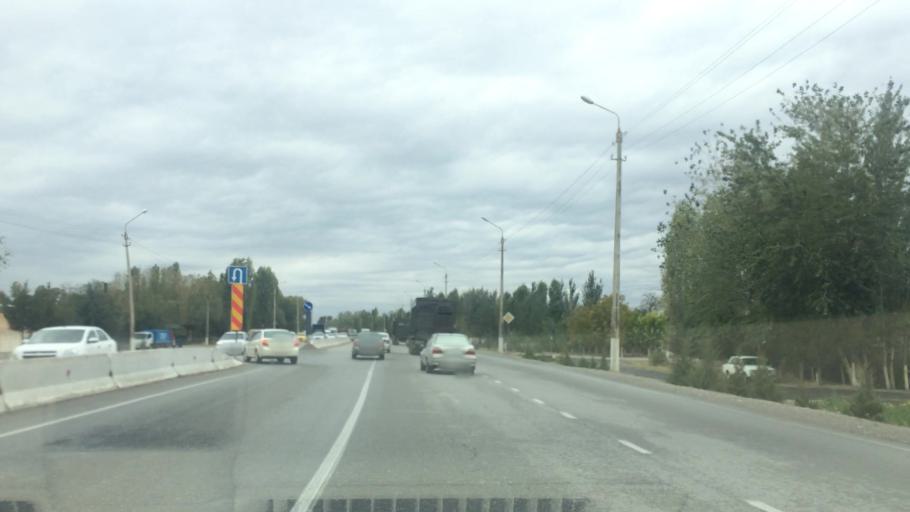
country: UZ
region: Jizzax
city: Jizzax
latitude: 39.9979
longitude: 67.5886
